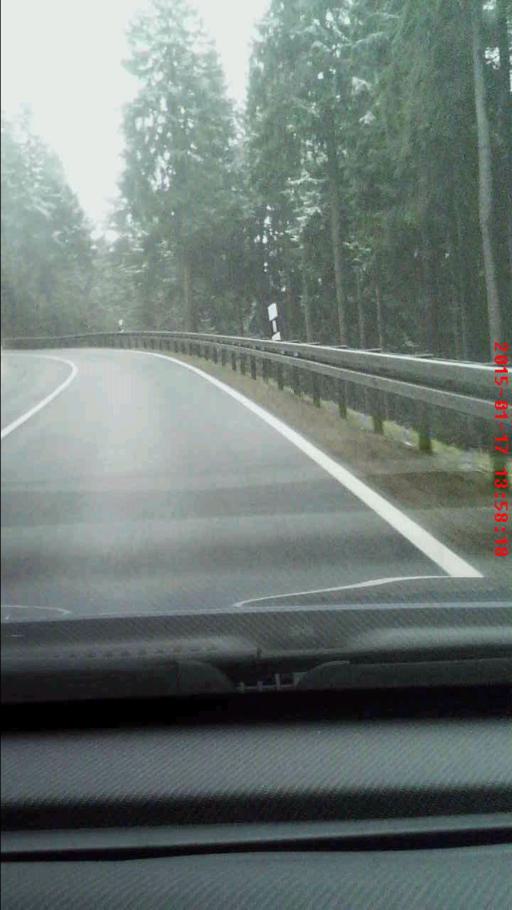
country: DE
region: Thuringia
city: Steinheid
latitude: 50.4704
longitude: 11.0747
